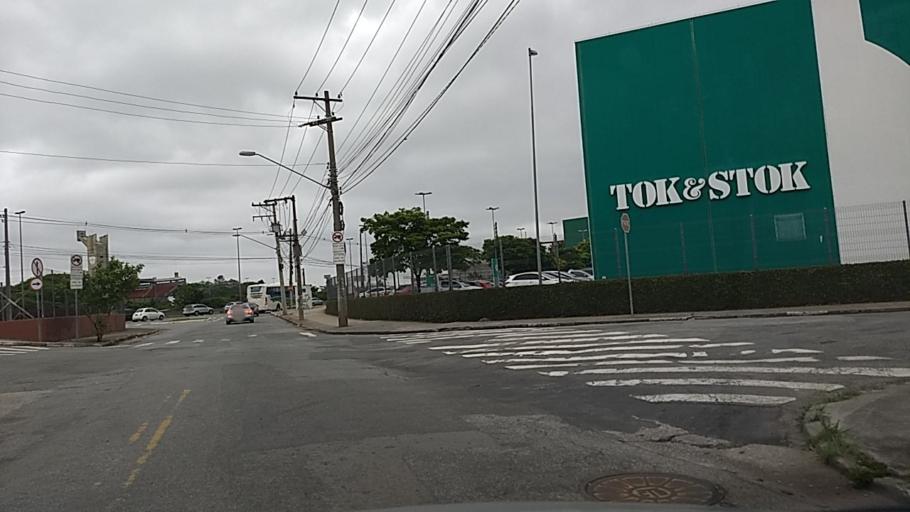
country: BR
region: Sao Paulo
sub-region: Sao Paulo
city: Sao Paulo
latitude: -23.5188
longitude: -46.6149
